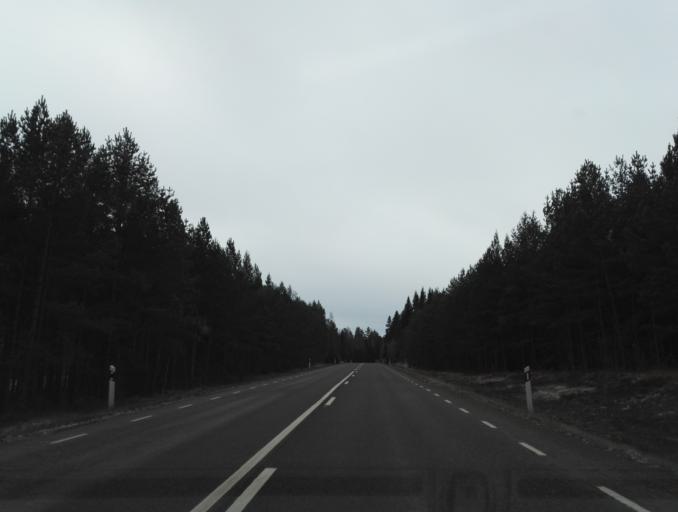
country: SE
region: Kalmar
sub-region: Hultsfreds Kommun
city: Virserum
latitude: 57.3396
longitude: 15.6032
